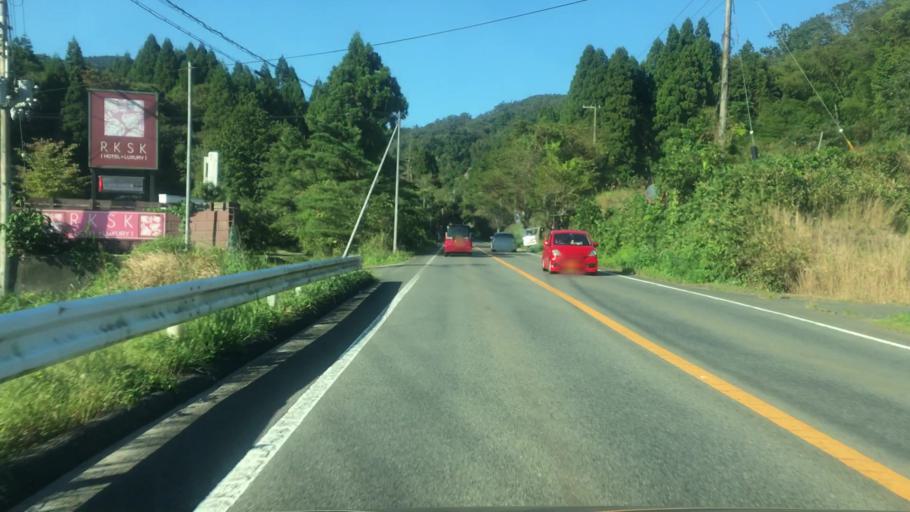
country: JP
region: Hyogo
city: Toyooka
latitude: 35.5627
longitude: 134.8520
